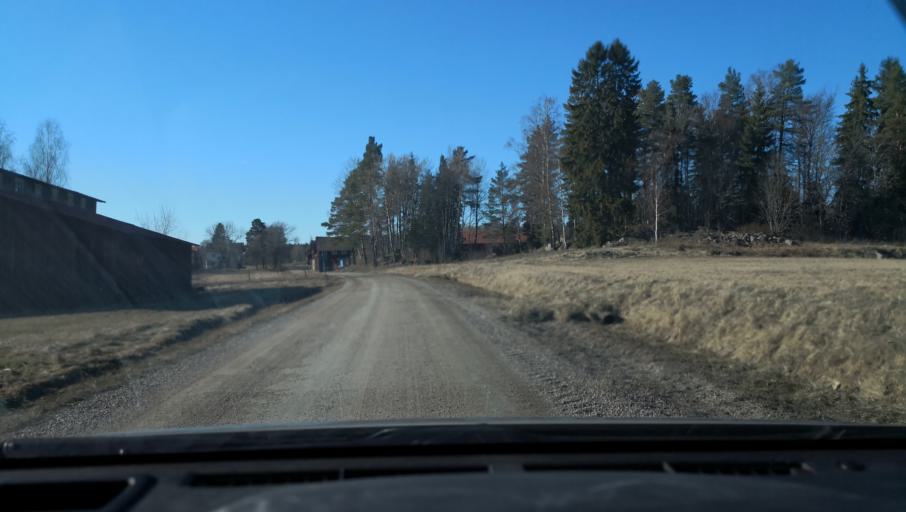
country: SE
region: Vaestmanland
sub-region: Sala Kommun
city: Sala
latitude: 60.1509
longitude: 16.6382
